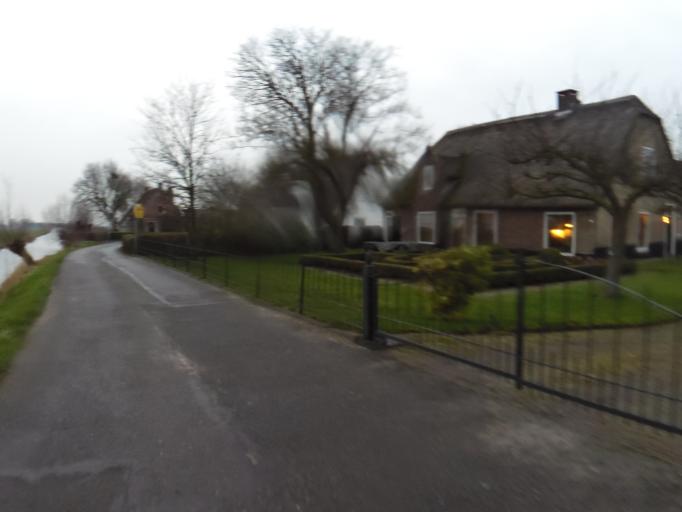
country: NL
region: South Holland
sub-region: Gemeente Leiderdorp
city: Leiderdorp
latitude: 52.1943
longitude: 4.5583
